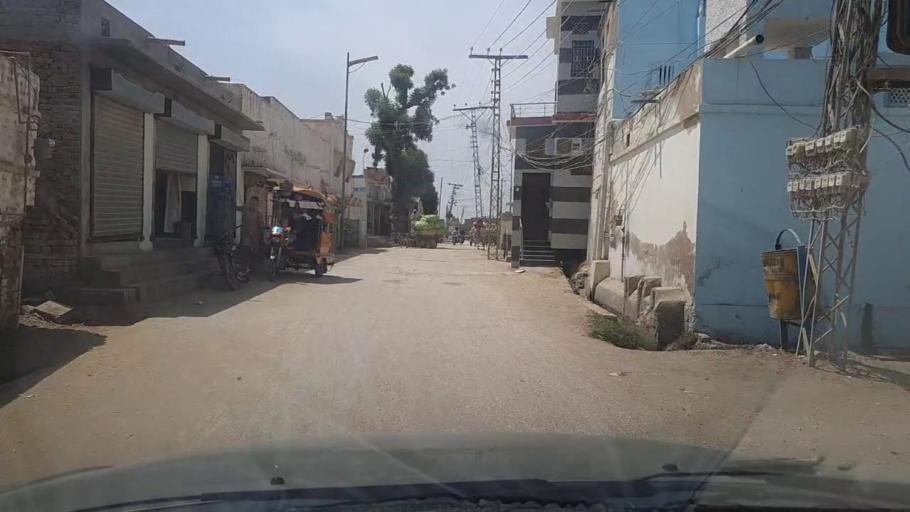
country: PK
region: Sindh
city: Bhiria
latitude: 26.9081
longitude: 68.1926
